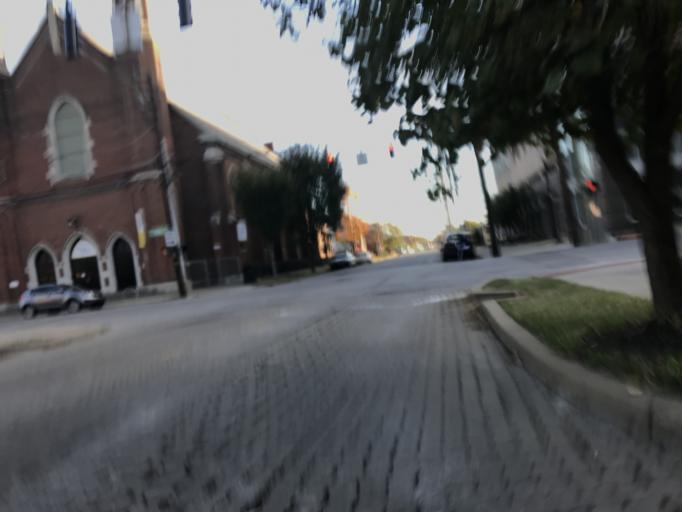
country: US
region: Kentucky
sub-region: Jefferson County
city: Louisville
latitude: 38.2495
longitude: -85.7408
